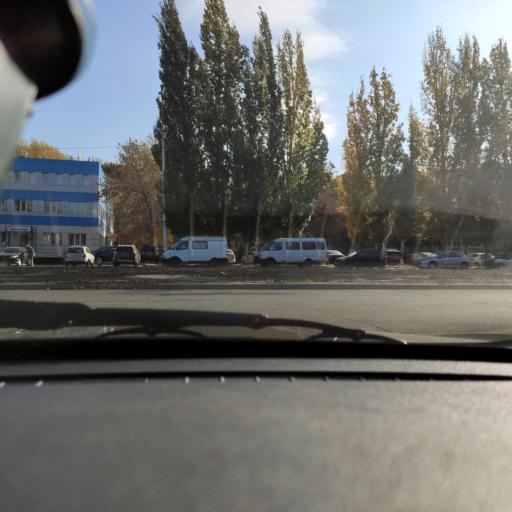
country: RU
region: Samara
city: Tol'yatti
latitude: 53.5166
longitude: 49.2853
